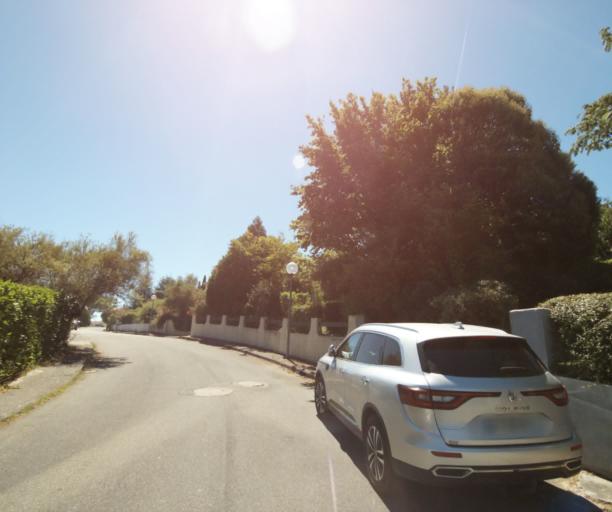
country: FR
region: Midi-Pyrenees
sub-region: Departement de la Haute-Garonne
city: Castanet-Tolosan
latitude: 43.5112
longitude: 1.4980
